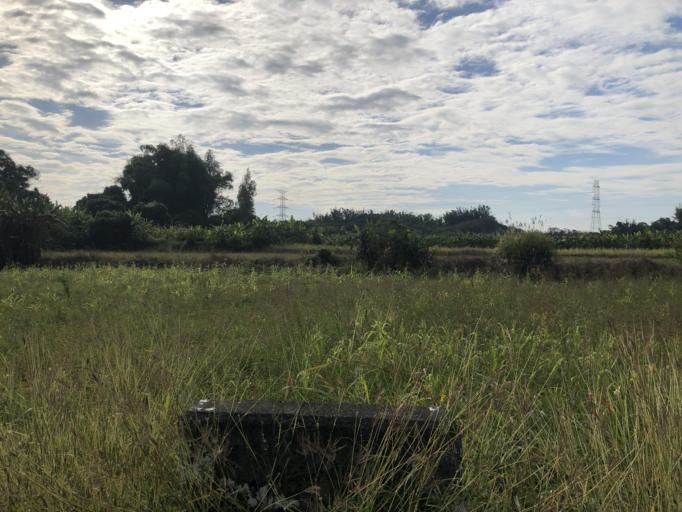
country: TW
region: Taiwan
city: Yujing
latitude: 23.0426
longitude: 120.4231
